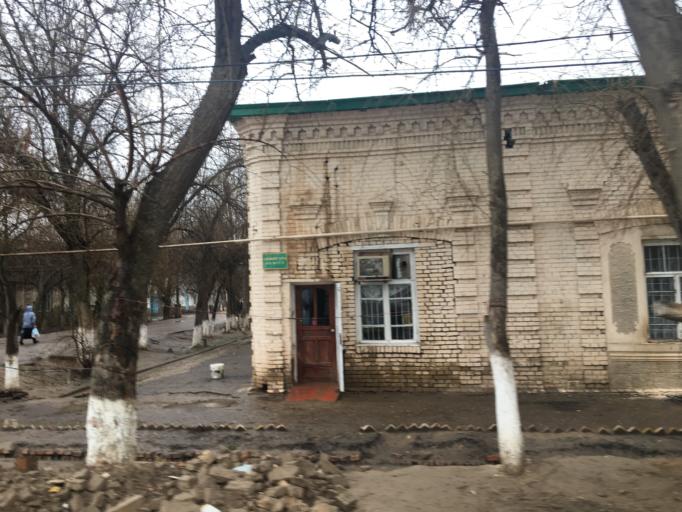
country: TM
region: Mary
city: Yoloeten
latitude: 37.3004
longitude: 62.3599
